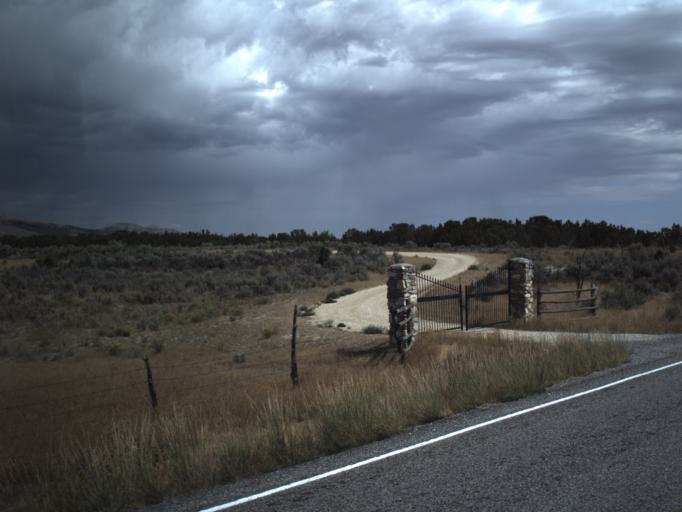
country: US
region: Idaho
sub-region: Cassia County
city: Burley
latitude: 41.8171
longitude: -113.3025
